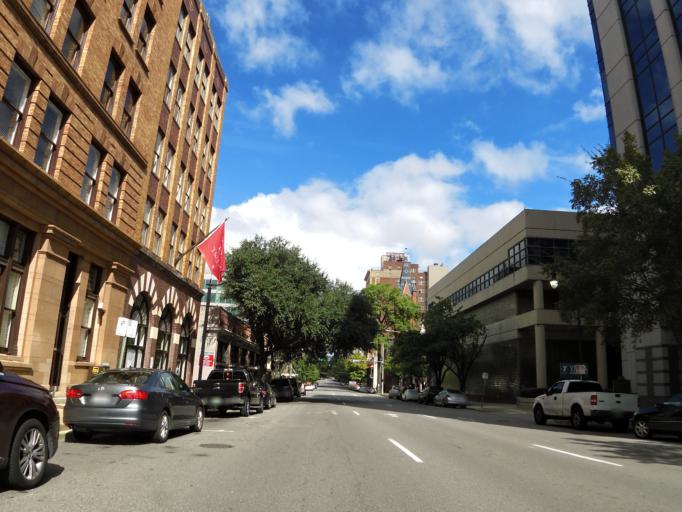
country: US
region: Alabama
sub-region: Jefferson County
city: Birmingham
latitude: 33.5170
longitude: -86.8057
